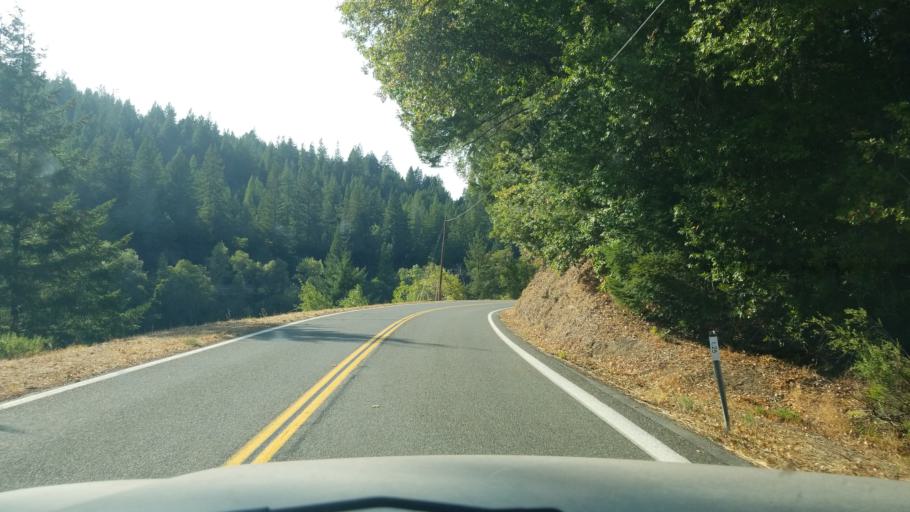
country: US
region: California
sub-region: Humboldt County
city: Redway
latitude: 40.1962
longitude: -123.7727
